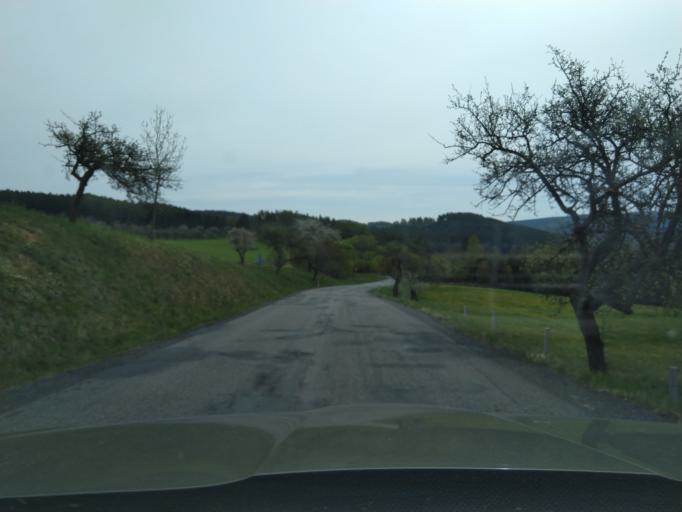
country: CZ
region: Plzensky
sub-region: Okres Klatovy
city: Kasperske Hory
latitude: 49.1966
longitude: 13.6175
